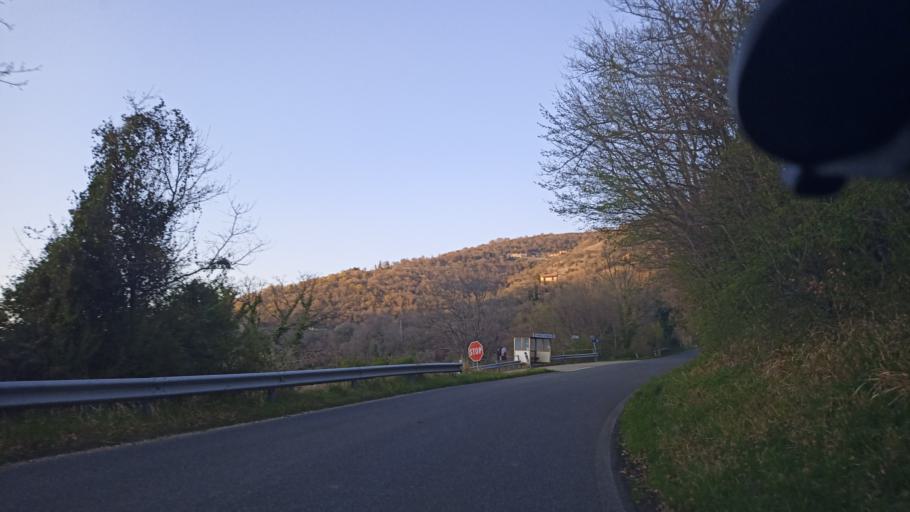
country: IT
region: Latium
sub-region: Provincia di Rieti
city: Cottanello
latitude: 42.4061
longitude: 12.6799
